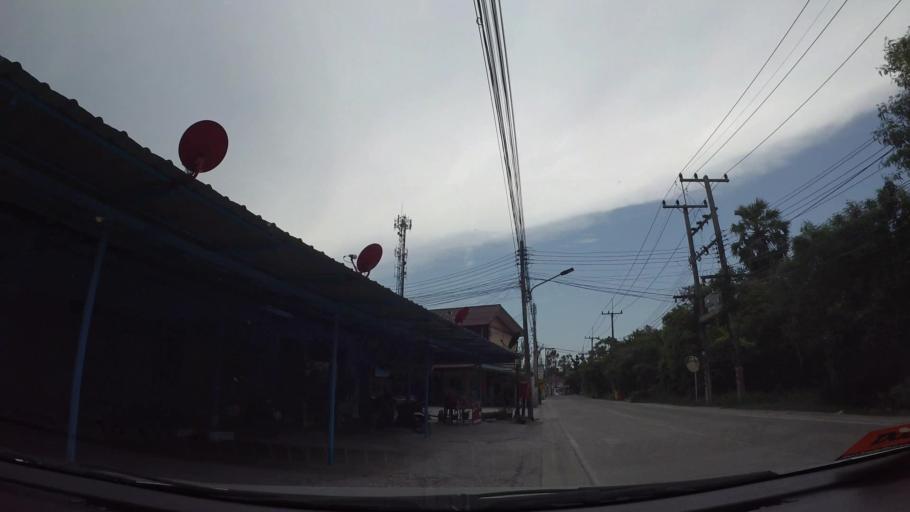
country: TH
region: Chon Buri
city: Chon Buri
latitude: 13.3318
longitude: 100.9648
